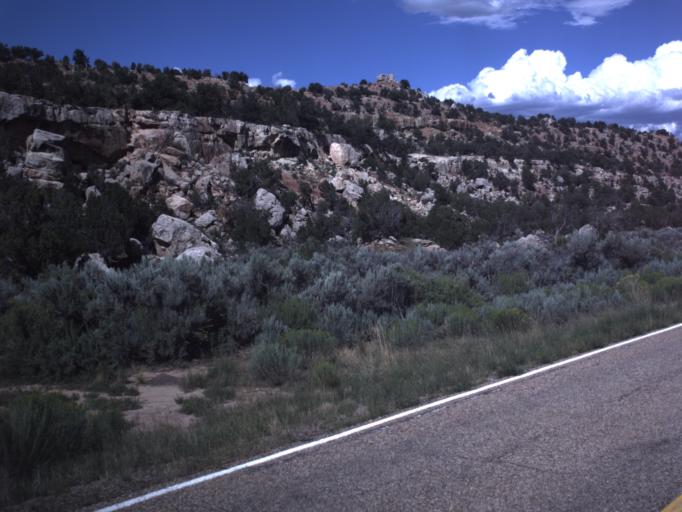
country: US
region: Utah
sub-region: Duchesne County
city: Duchesne
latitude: 40.3212
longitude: -110.6902
